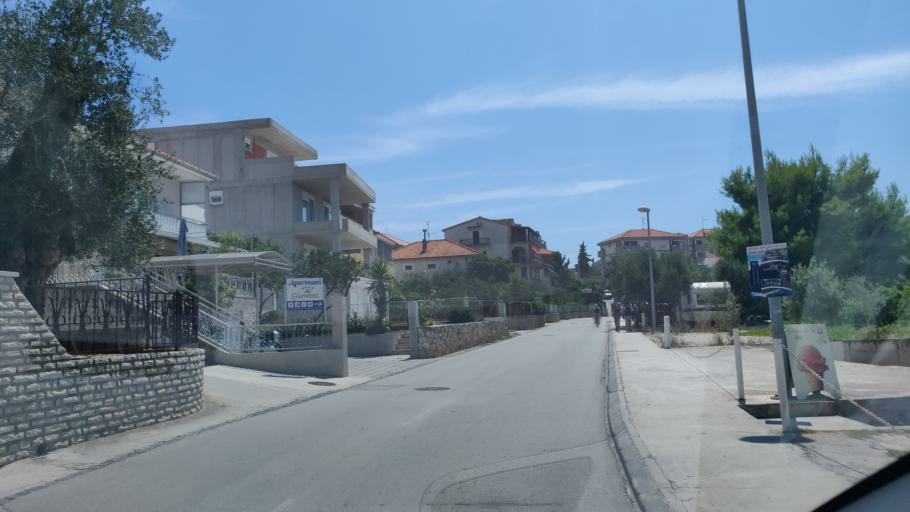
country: HR
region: Splitsko-Dalmatinska
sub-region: Grad Trogir
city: Trogir
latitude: 43.5068
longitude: 16.2594
